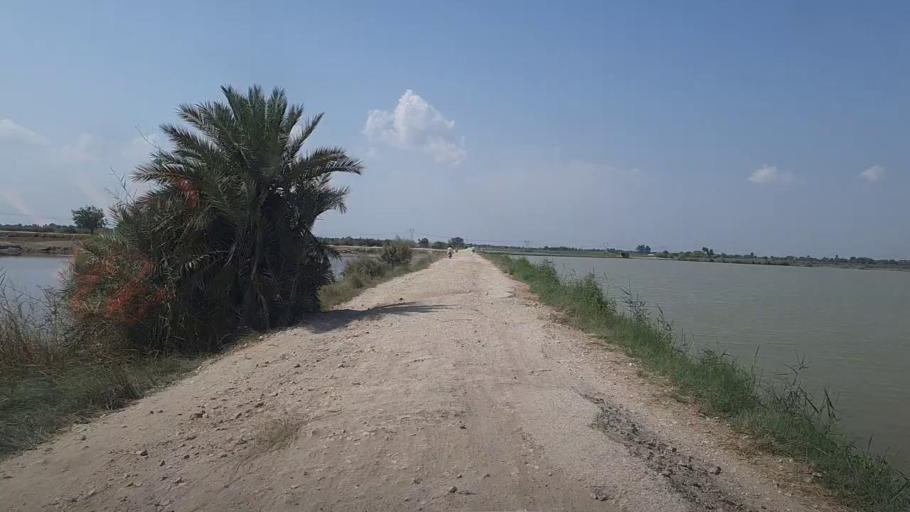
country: PK
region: Sindh
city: Khairpur
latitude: 28.0963
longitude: 69.6280
